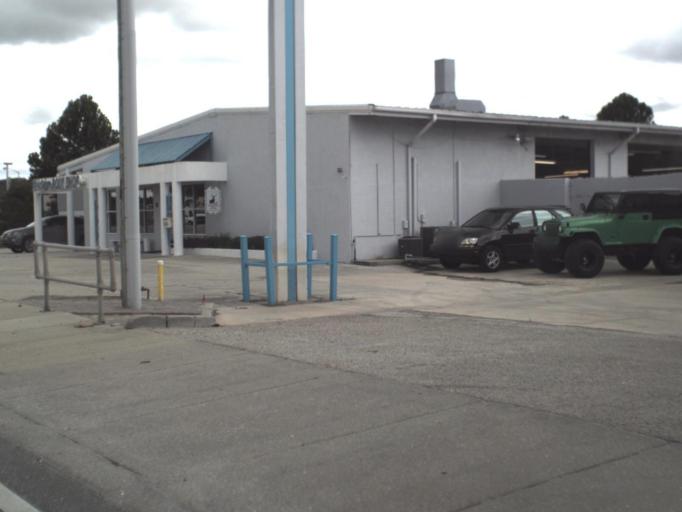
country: US
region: Florida
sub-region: Sarasota County
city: Bee Ridge
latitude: 27.2691
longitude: -82.4776
